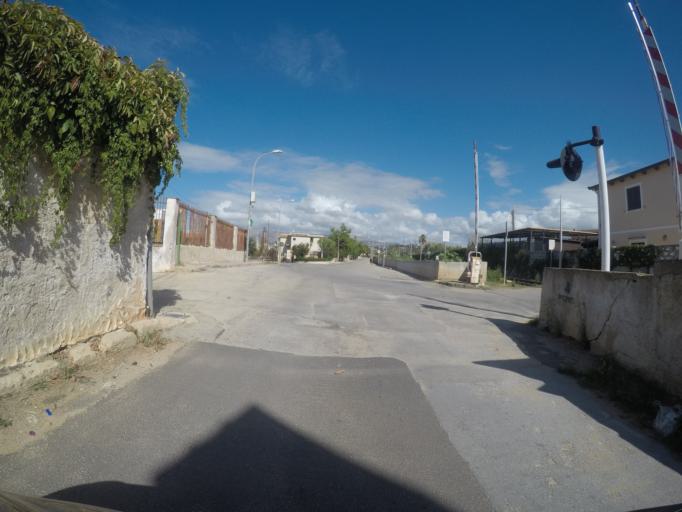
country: IT
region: Sicily
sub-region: Palermo
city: Trappeto
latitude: 38.0639
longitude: 13.0331
